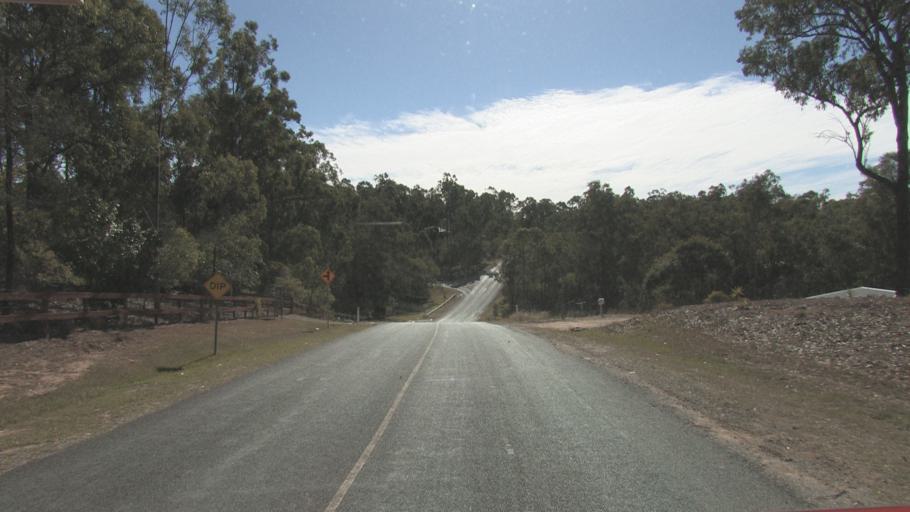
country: AU
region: Queensland
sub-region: Ipswich
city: Springfield Lakes
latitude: -27.7154
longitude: 152.9164
